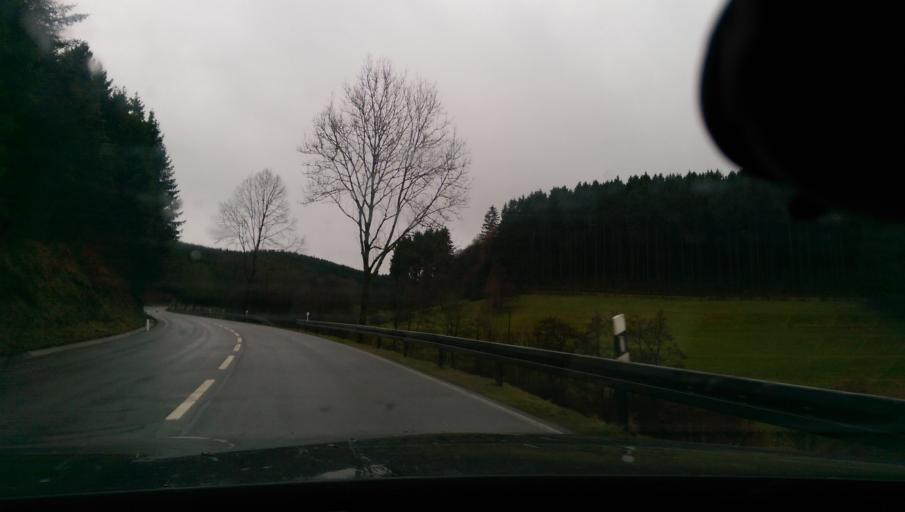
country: DE
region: North Rhine-Westphalia
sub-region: Regierungsbezirk Arnsberg
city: Sundern
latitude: 51.2529
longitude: 7.9705
